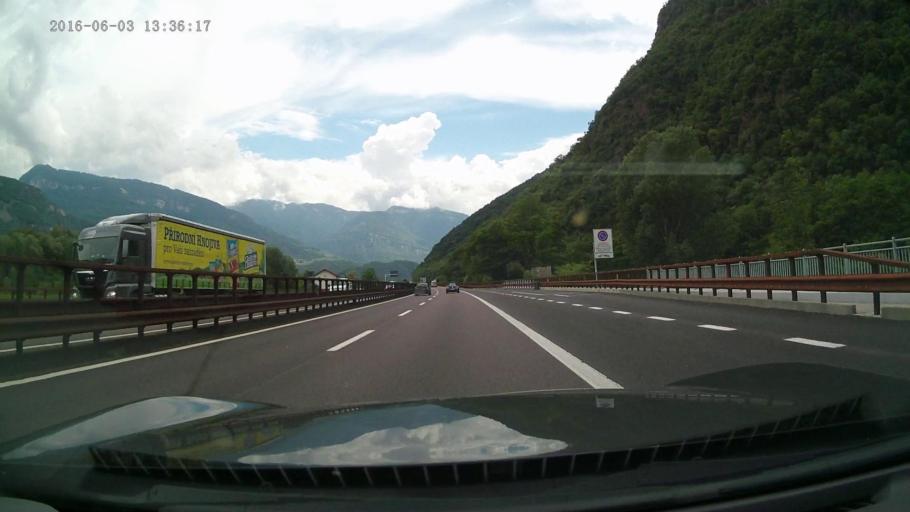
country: IT
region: Trentino-Alto Adige
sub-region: Bolzano
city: Ora
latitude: 46.3743
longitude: 11.2904
